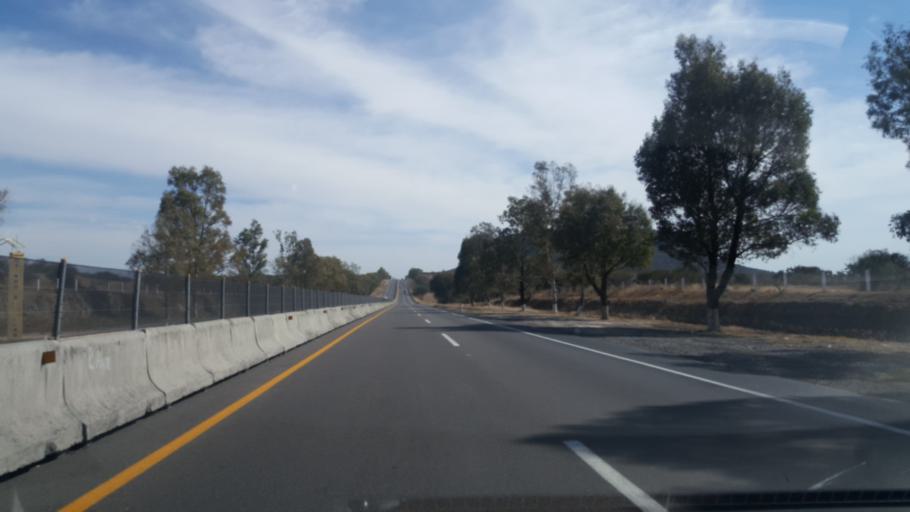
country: MX
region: Jalisco
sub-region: Lagos de Moreno
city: Cristeros [Fraccionamiento]
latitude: 21.3041
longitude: -102.0238
